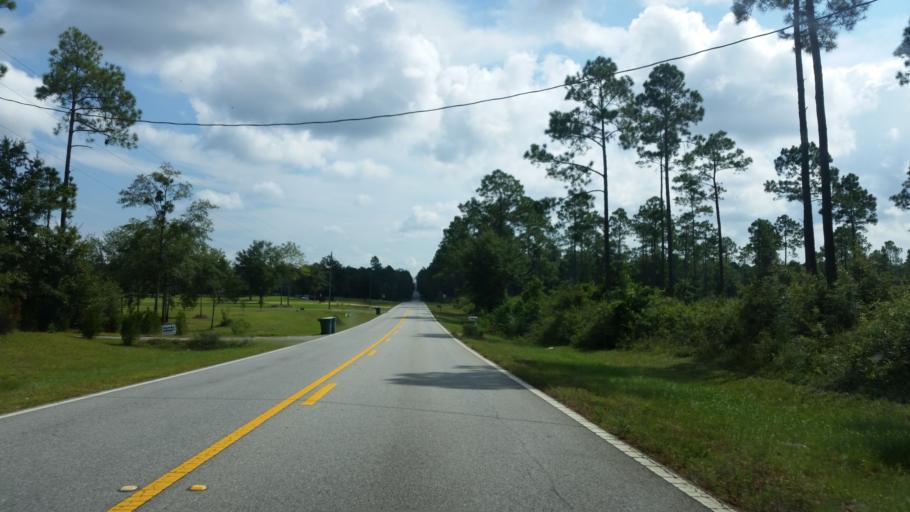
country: US
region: Florida
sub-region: Escambia County
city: Molino
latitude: 30.6816
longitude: -87.3930
